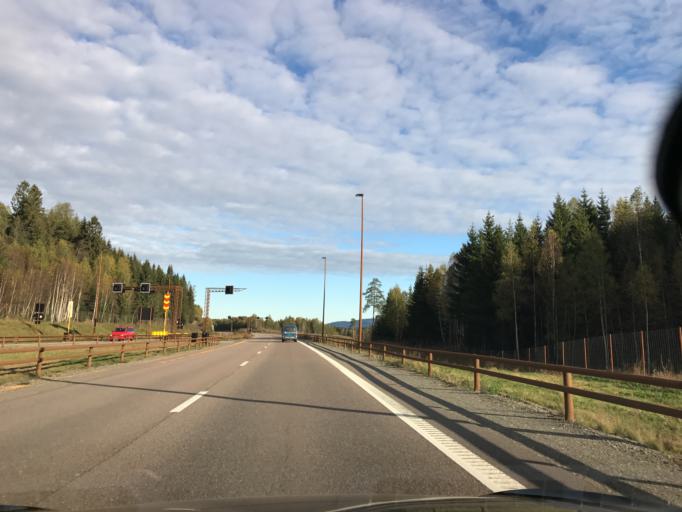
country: NO
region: Akershus
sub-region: Eidsvoll
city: Eidsvoll
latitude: 60.3473
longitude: 11.2089
